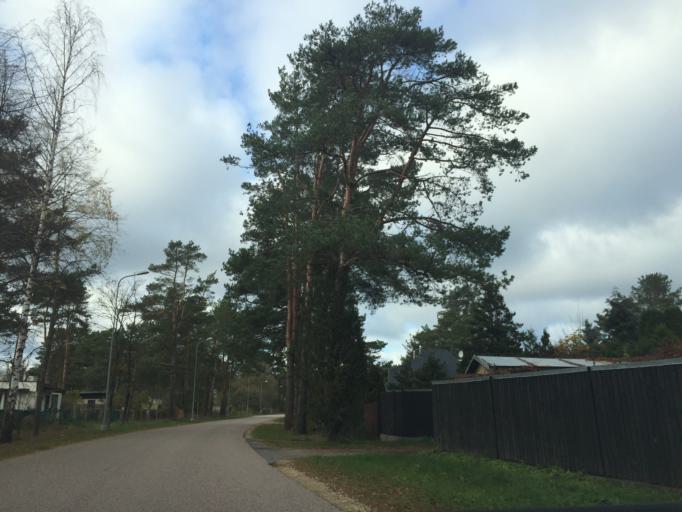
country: LV
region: Carnikava
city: Carnikava
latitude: 57.1256
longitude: 24.3142
